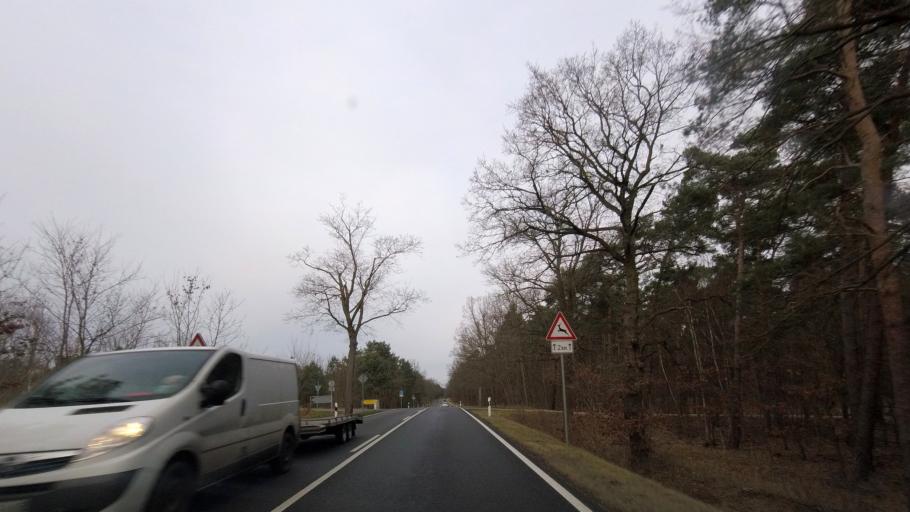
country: DE
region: Brandenburg
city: Treuenbrietzen
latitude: 52.0646
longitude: 12.8950
